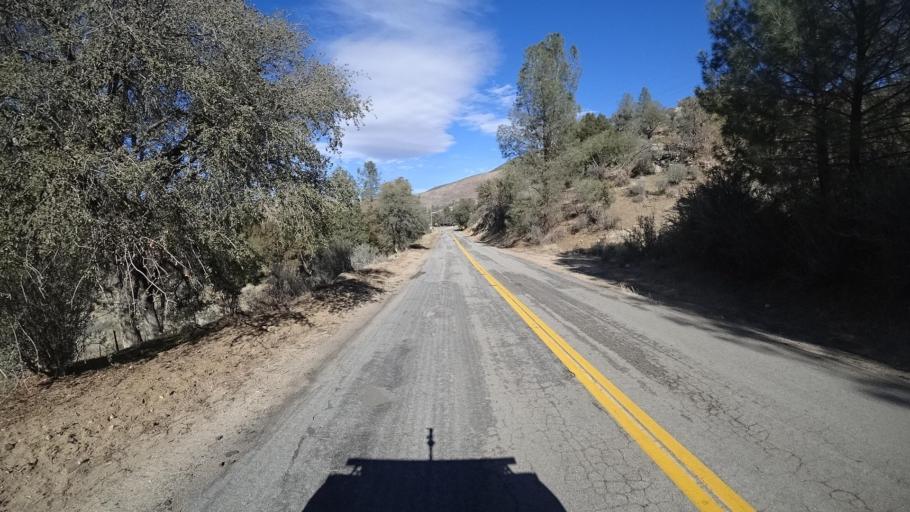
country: US
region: California
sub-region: Kern County
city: Bodfish
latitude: 35.5334
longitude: -118.5119
